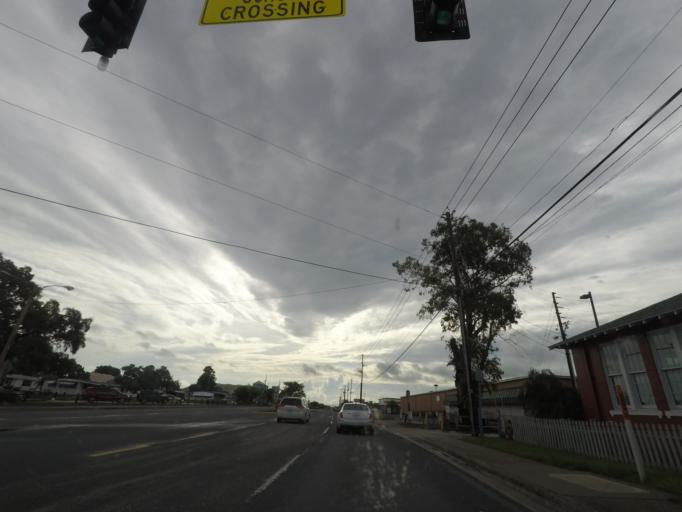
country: US
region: Florida
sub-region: Pinellas County
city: Seminole
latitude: 27.8396
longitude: -82.7915
